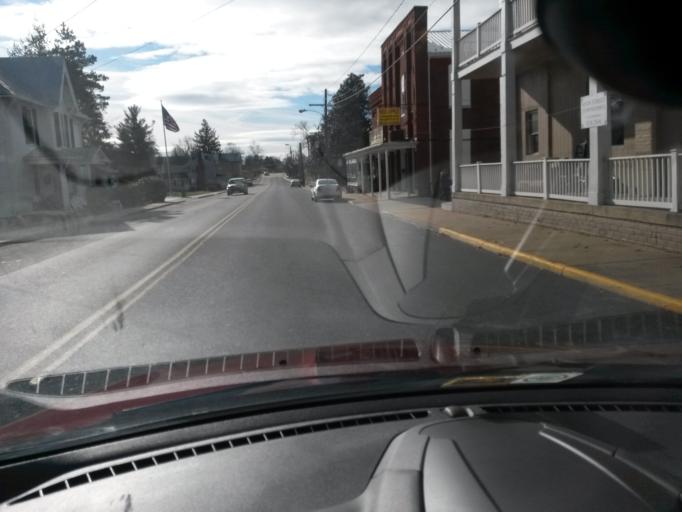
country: US
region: Virginia
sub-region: Rockingham County
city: Bridgewater
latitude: 38.3811
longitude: -78.9779
